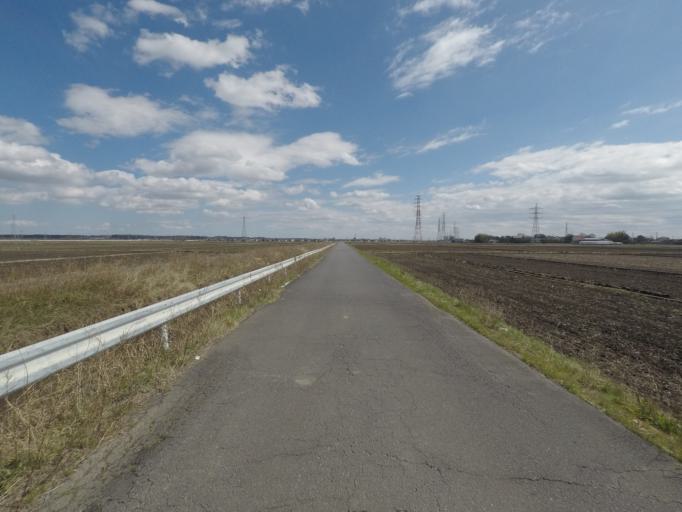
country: JP
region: Ibaraki
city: Fujishiro
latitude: 35.9408
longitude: 140.1073
